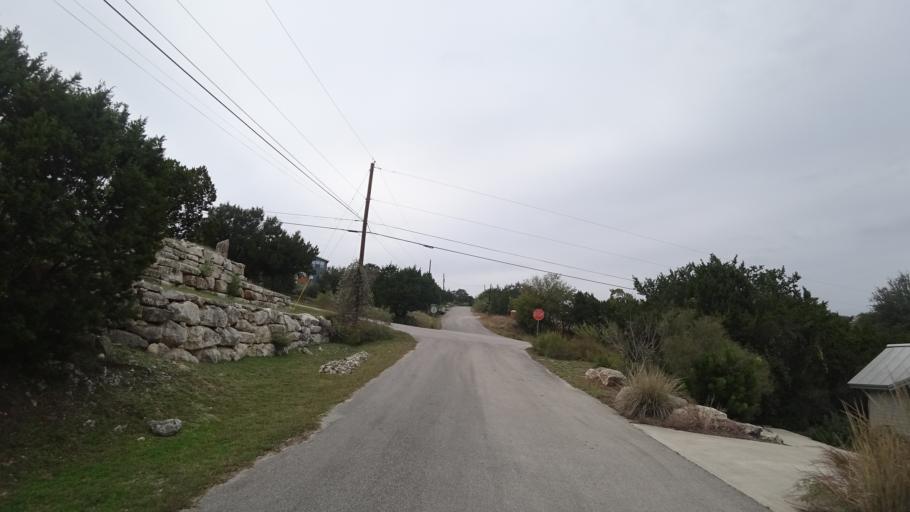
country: US
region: Texas
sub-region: Travis County
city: Hudson Bend
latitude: 30.3693
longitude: -97.9186
